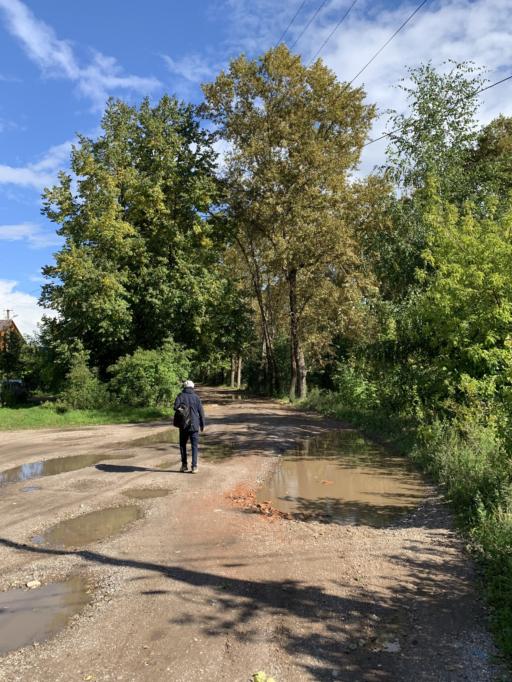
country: RU
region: Tverskaya
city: Vyshniy Volochek
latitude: 57.5788
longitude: 34.5599
